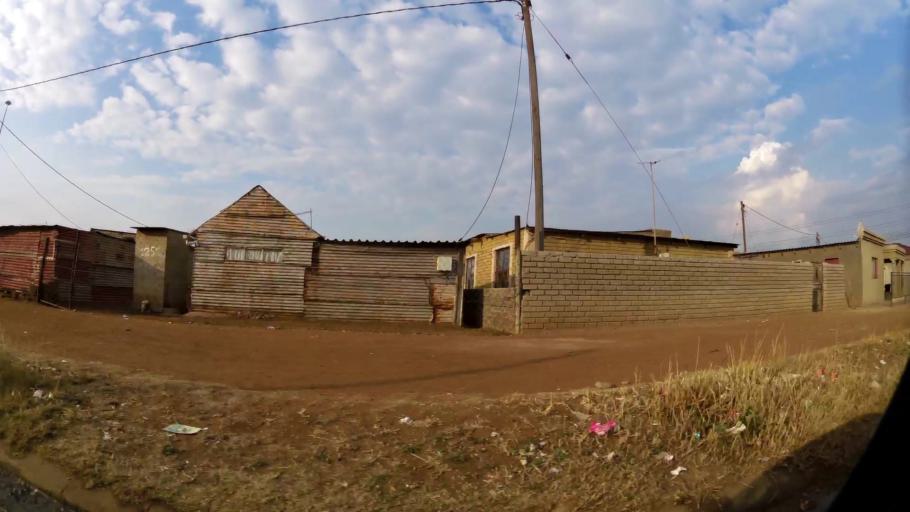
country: ZA
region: Gauteng
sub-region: Sedibeng District Municipality
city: Vanderbijlpark
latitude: -26.6793
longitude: 27.8695
